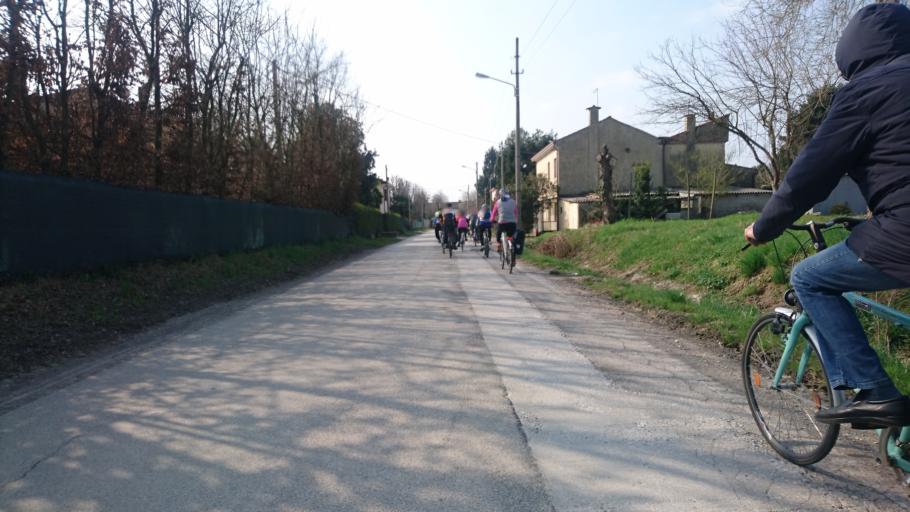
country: IT
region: Veneto
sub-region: Provincia di Padova
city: Mandriola-Sant'Agostino
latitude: 45.3822
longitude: 11.8330
